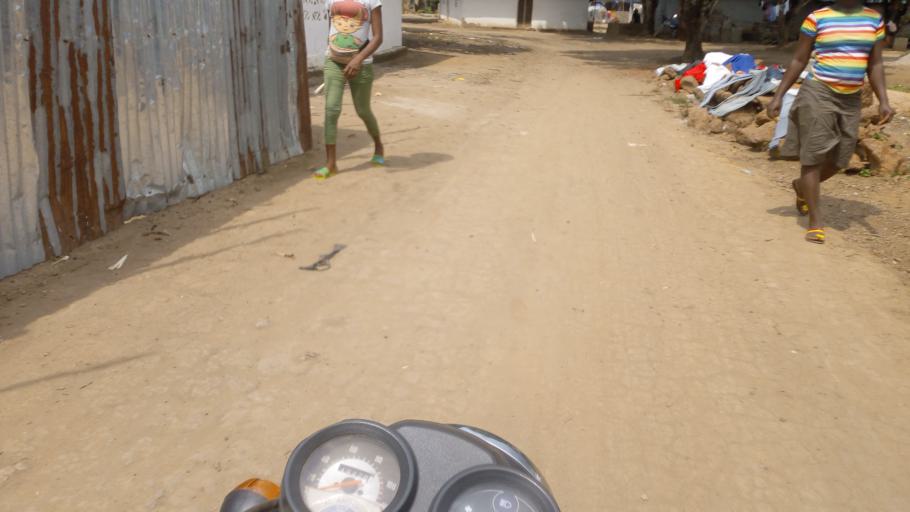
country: SL
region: Western Area
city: Waterloo
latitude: 8.3088
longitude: -13.0648
